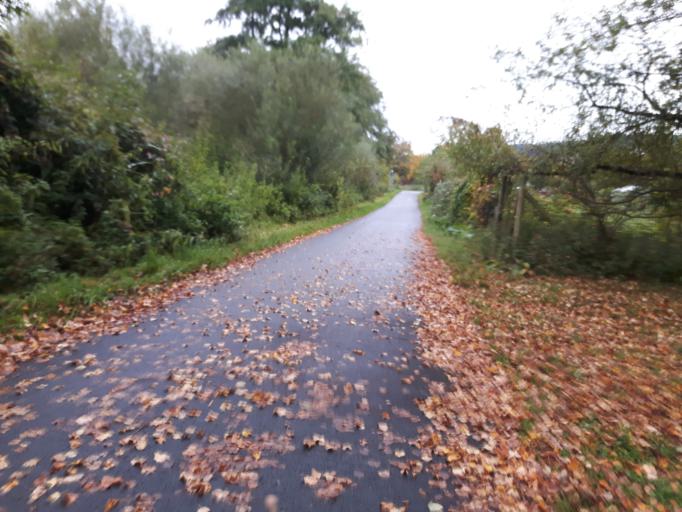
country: DE
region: Bavaria
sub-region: Regierungsbezirk Unterfranken
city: Erlabrunn
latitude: 49.8651
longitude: 9.8409
